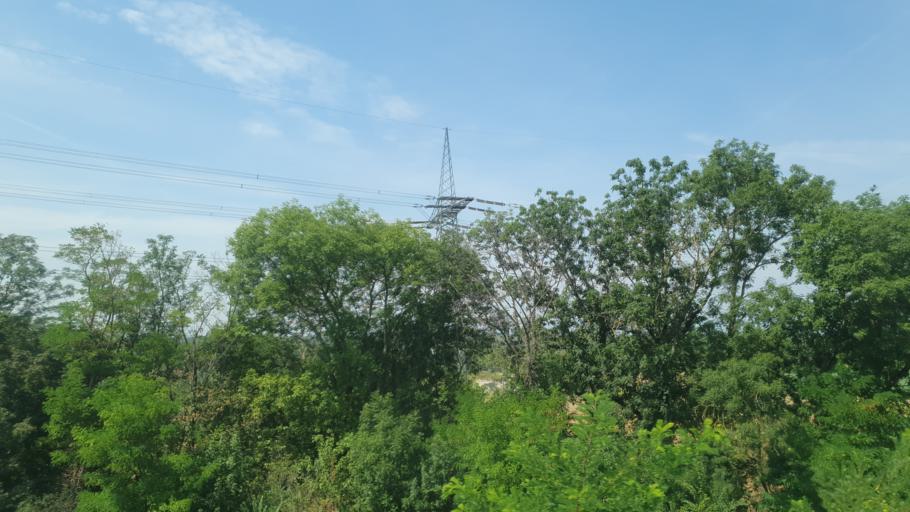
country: DE
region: Baden-Wuerttemberg
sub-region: Freiburg Region
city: Bad Bellingen
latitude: 47.7480
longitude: 7.5612
